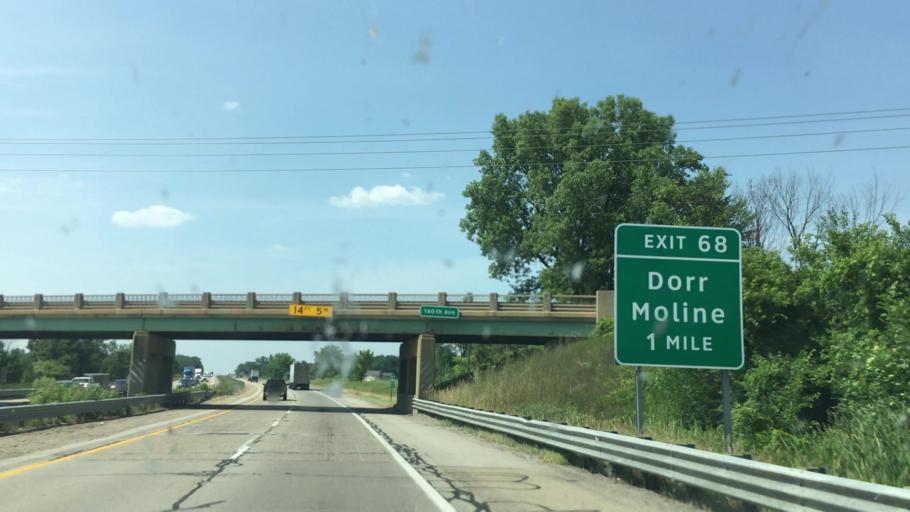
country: US
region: Michigan
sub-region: Allegan County
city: Wayland
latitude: 42.7099
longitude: -85.6610
